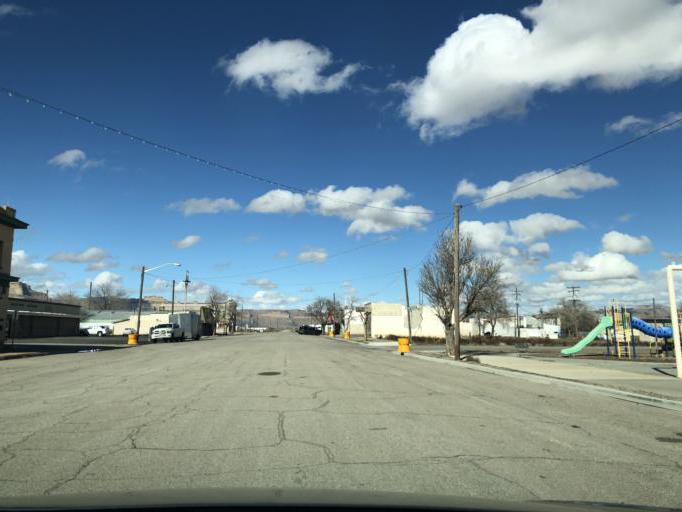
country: US
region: Utah
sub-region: Carbon County
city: East Carbon City
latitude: 38.9937
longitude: -110.1651
